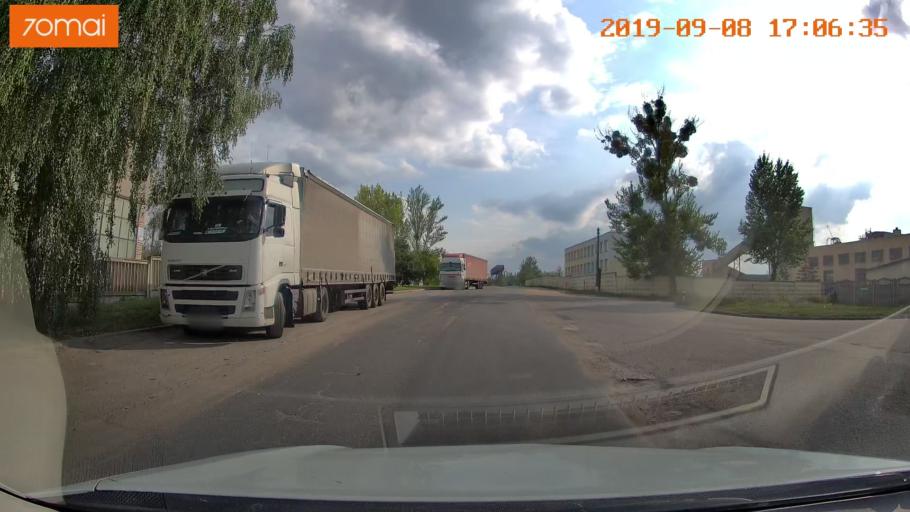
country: BY
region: Grodnenskaya
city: Hrodna
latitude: 53.6695
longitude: 23.9524
